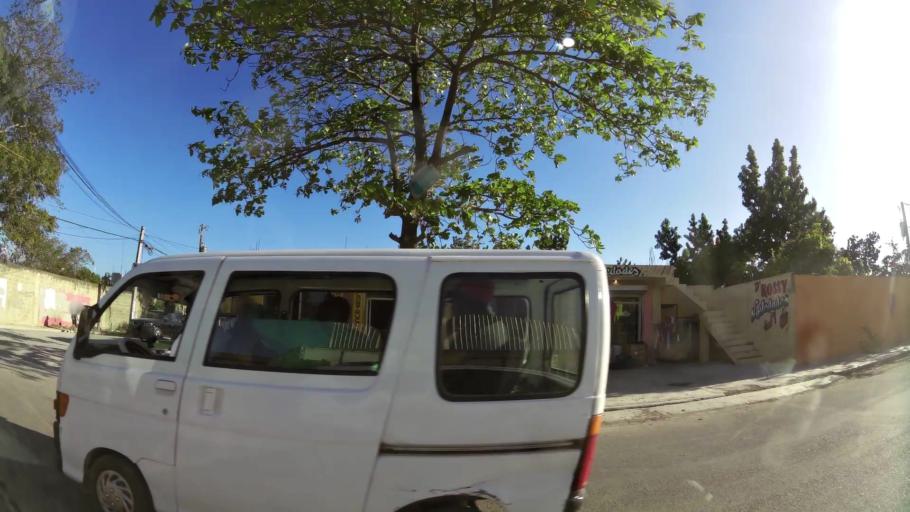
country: DO
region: Santo Domingo
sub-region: Santo Domingo
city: Santo Domingo Este
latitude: 18.4808
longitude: -69.8229
